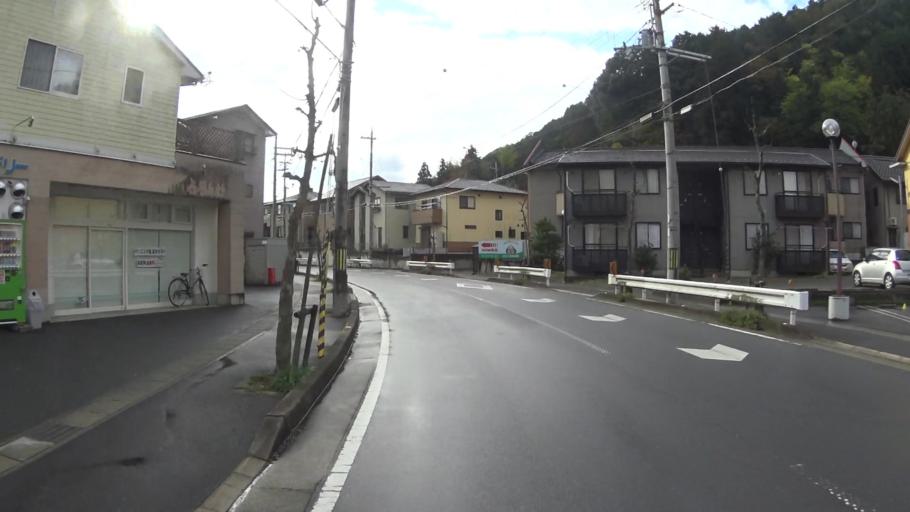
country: JP
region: Kyoto
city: Ayabe
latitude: 35.3014
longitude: 135.2319
